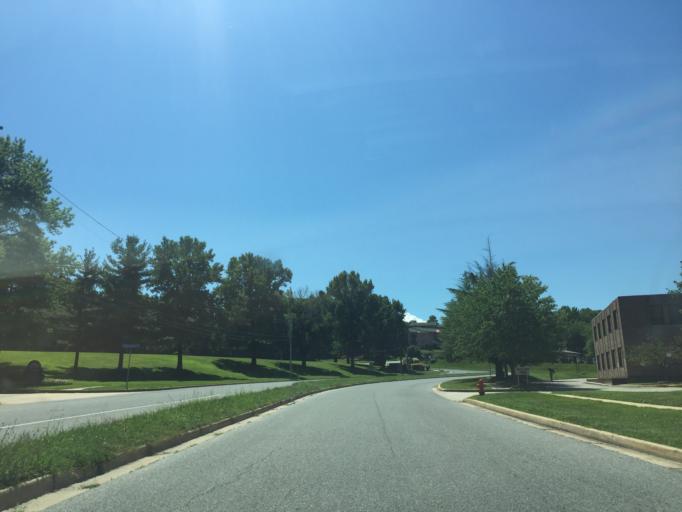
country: US
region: Maryland
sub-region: Baltimore County
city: Cockeysville
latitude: 39.4729
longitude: -76.6204
